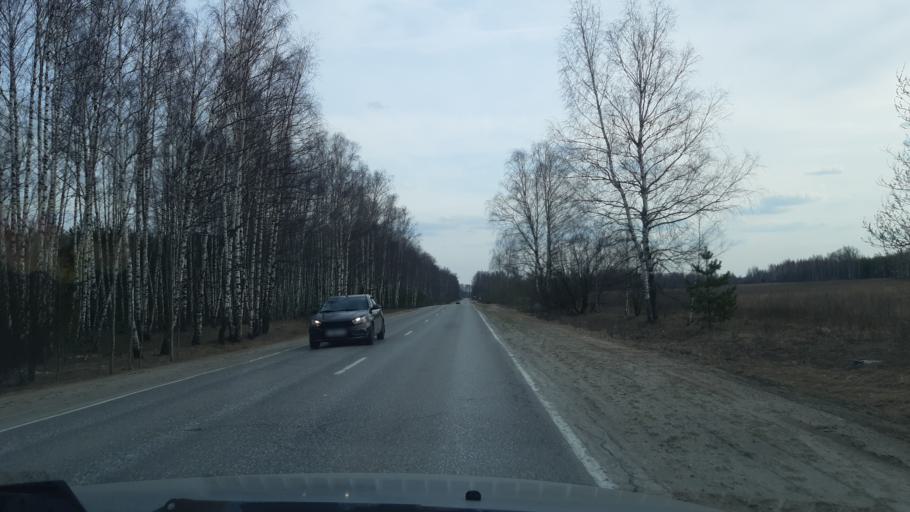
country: RU
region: Vladimir
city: Luknovo
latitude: 56.2328
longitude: 42.0344
